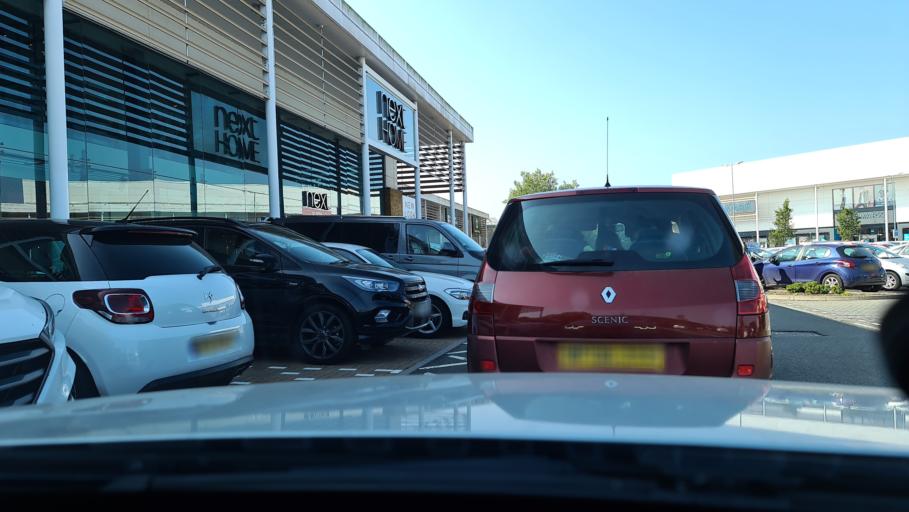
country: GB
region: England
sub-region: Oxfordshire
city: Banbury
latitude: 52.0764
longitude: -1.3186
